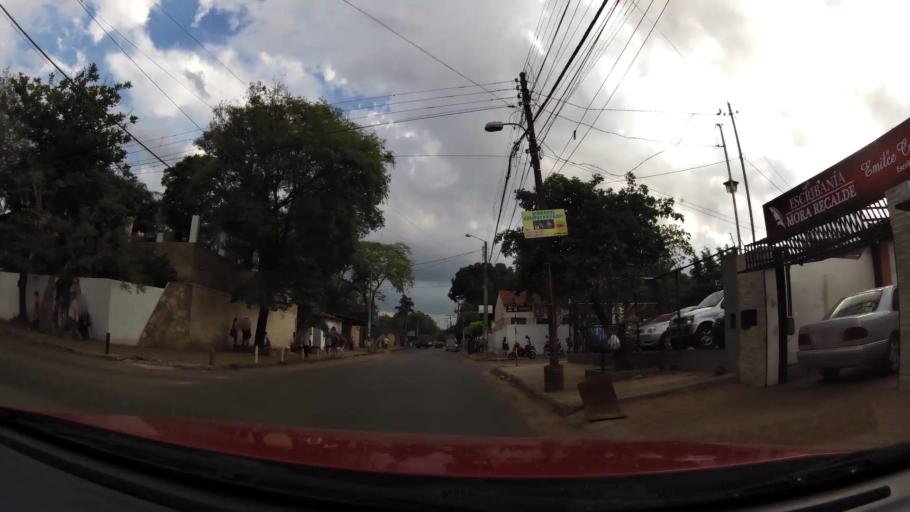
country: PY
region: Central
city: Fernando de la Mora
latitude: -25.3377
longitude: -57.5437
